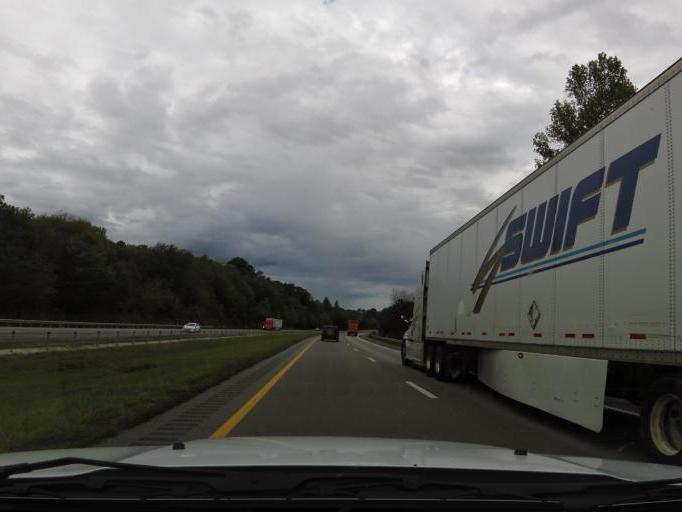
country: US
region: Kentucky
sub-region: Whitley County
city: Corbin
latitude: 36.8804
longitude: -84.1503
